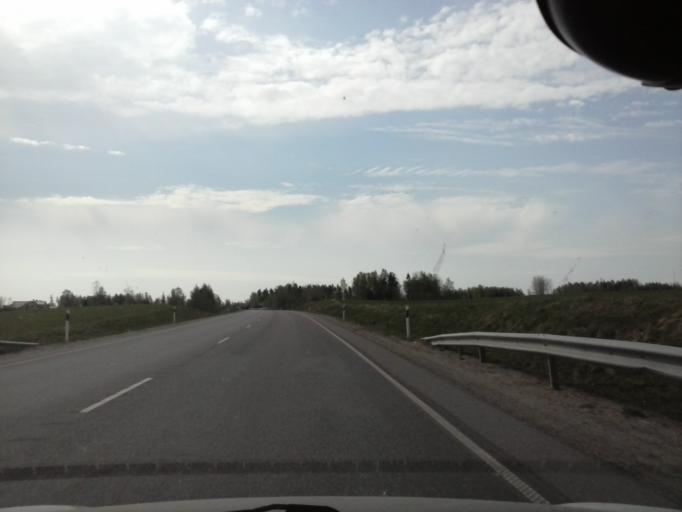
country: EE
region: Tartu
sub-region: UElenurme vald
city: Ulenurme
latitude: 58.1513
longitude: 26.6956
